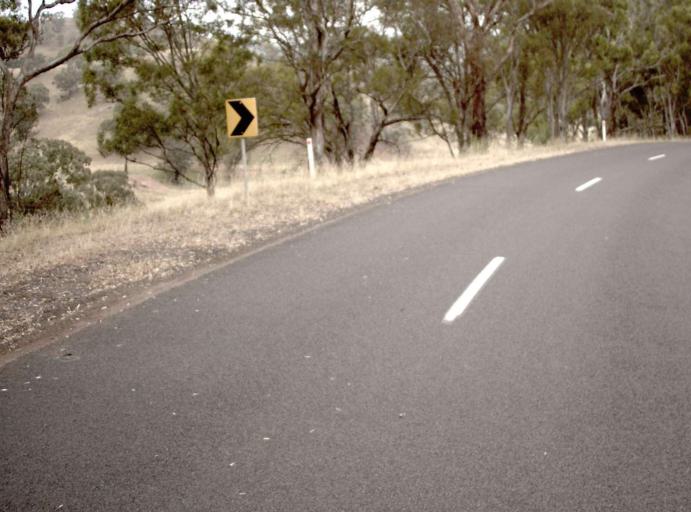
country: AU
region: Victoria
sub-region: Wellington
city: Heyfield
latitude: -37.6888
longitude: 146.6547
